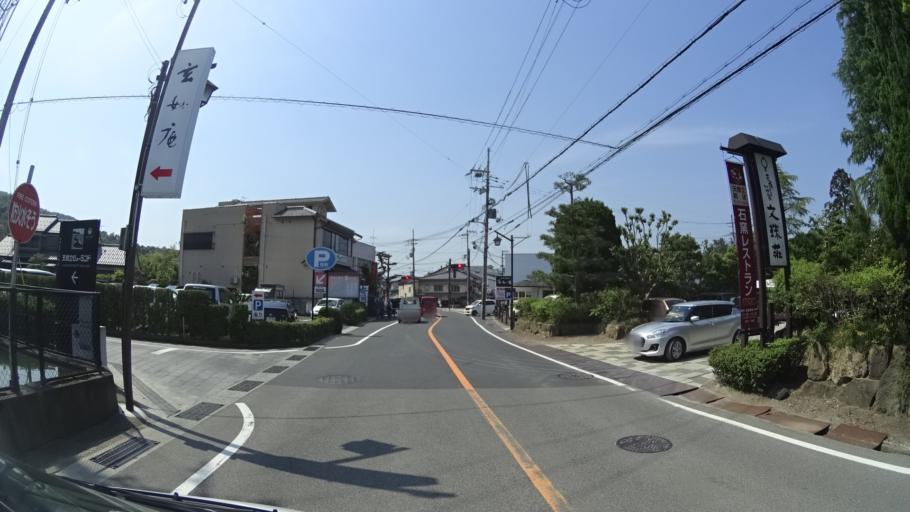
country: JP
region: Kyoto
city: Miyazu
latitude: 35.5563
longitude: 135.1853
